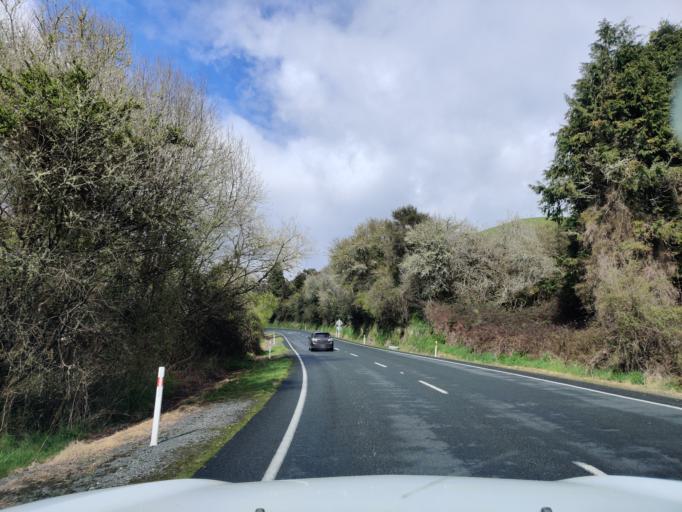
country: NZ
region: Waikato
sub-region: Otorohanga District
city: Otorohanga
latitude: -38.5980
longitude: 175.2173
